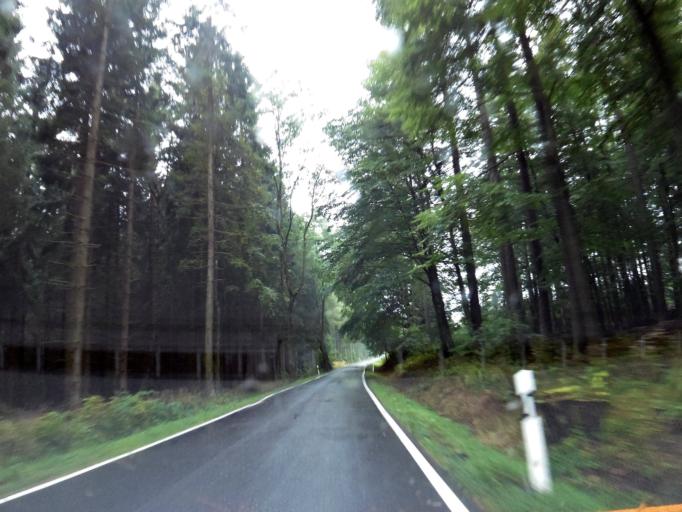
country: DE
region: Saxony-Anhalt
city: Hasselfelde
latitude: 51.6559
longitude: 10.8464
